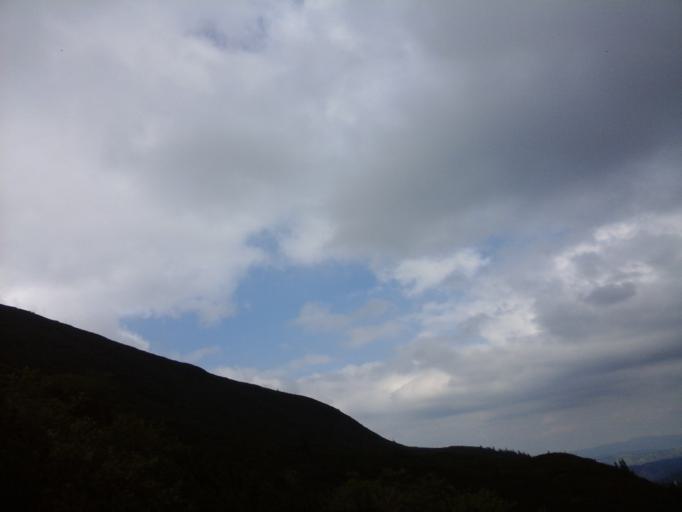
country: PL
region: Lesser Poland Voivodeship
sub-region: Powiat tatrzanski
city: Zakopane
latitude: 49.2405
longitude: 20.0004
